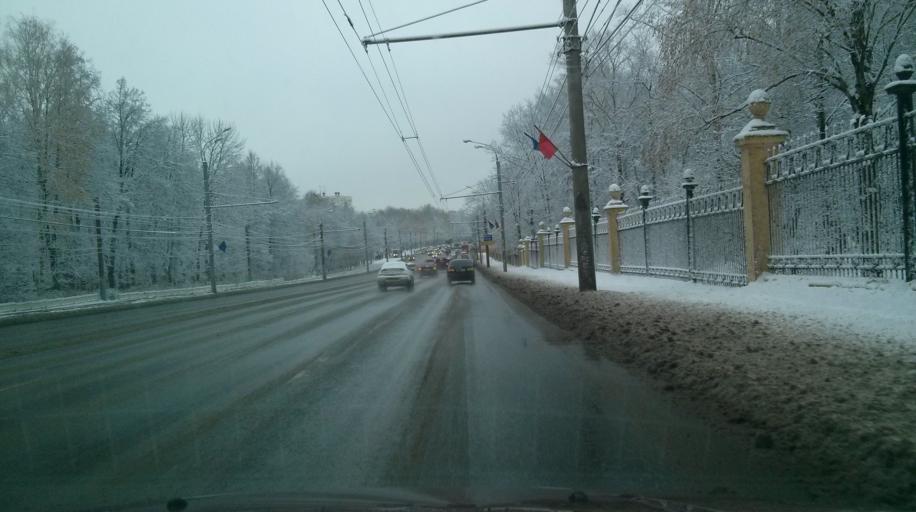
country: RU
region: Nizjnij Novgorod
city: Nizhniy Novgorod
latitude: 56.2645
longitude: 43.9746
